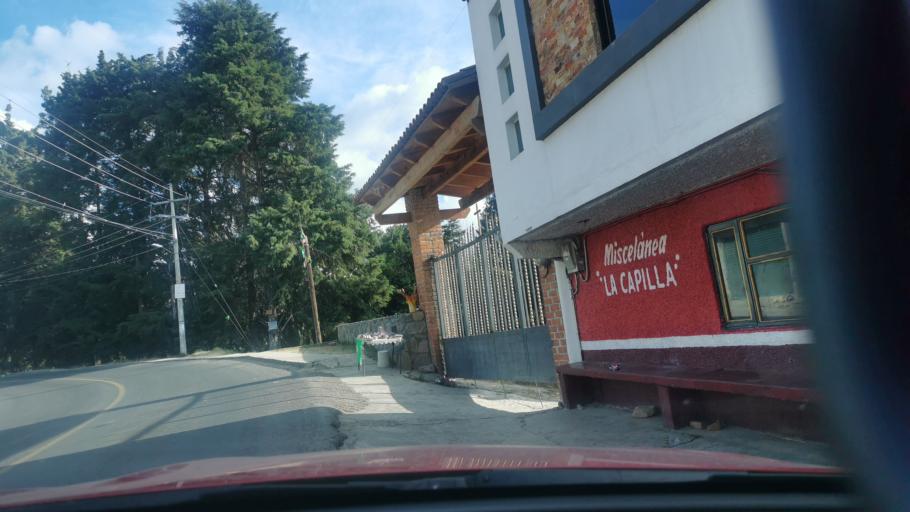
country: MX
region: Mexico
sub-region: Amanalco
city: Polvillos (San Bartolo Quinta Seccion)
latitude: 19.2358
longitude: -100.0795
